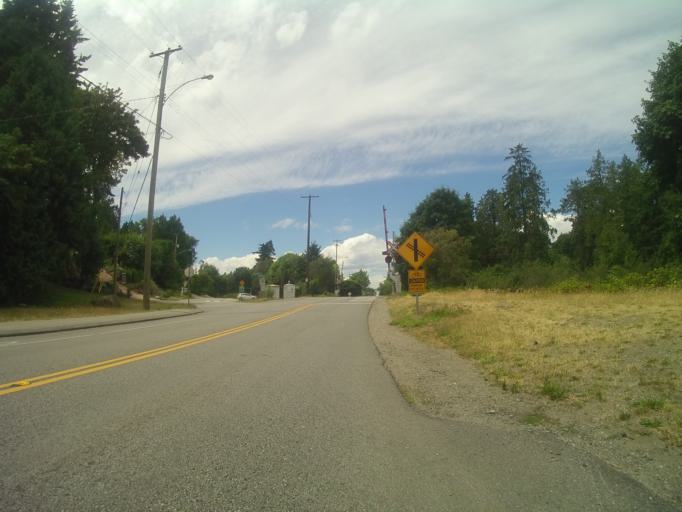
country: CA
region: British Columbia
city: Surrey
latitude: 49.0537
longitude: -122.8780
